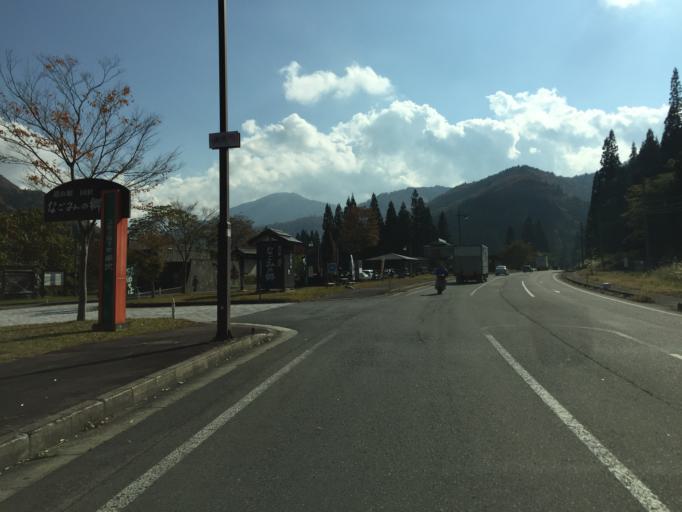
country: JP
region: Yamagata
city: Yonezawa
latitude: 37.8778
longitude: 139.9837
